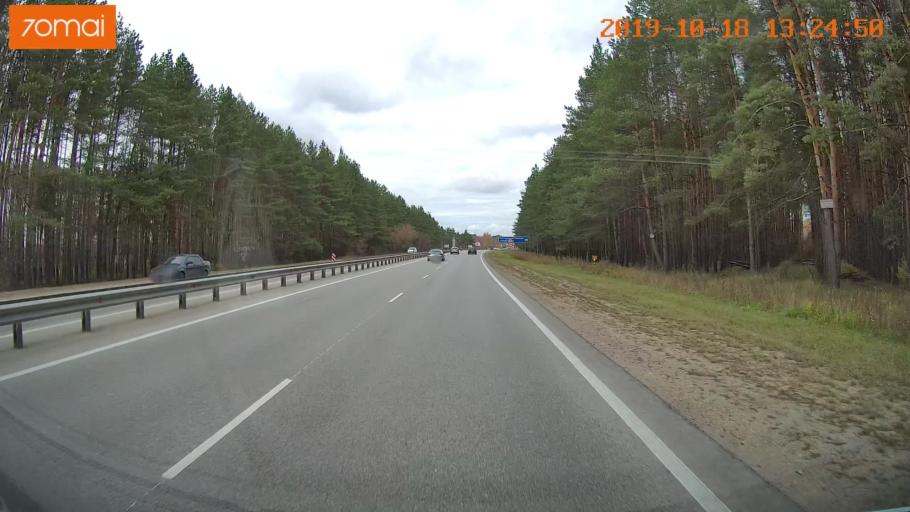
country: RU
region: Rjazan
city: Polyany
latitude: 54.7362
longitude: 39.8419
